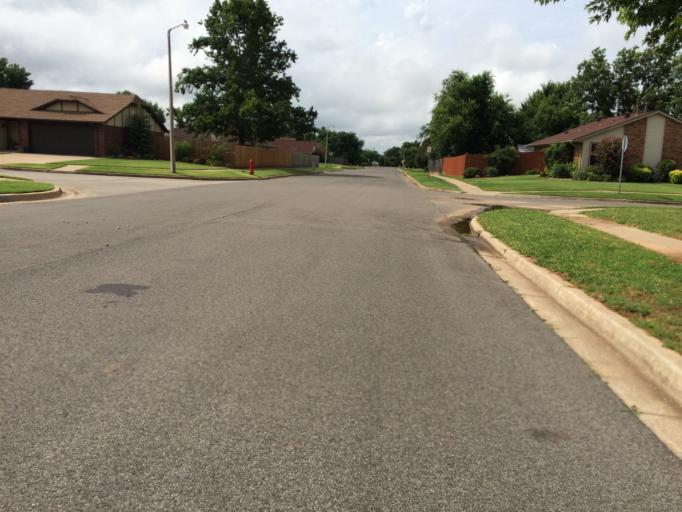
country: US
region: Oklahoma
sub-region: Cleveland County
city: Hall Park
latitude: 35.2215
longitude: -97.4134
